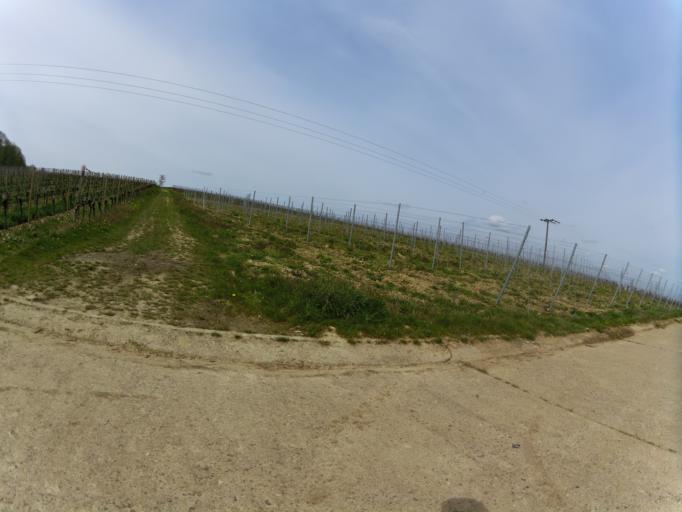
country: DE
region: Bavaria
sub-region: Regierungsbezirk Unterfranken
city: Nordheim
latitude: 49.8586
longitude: 10.1658
